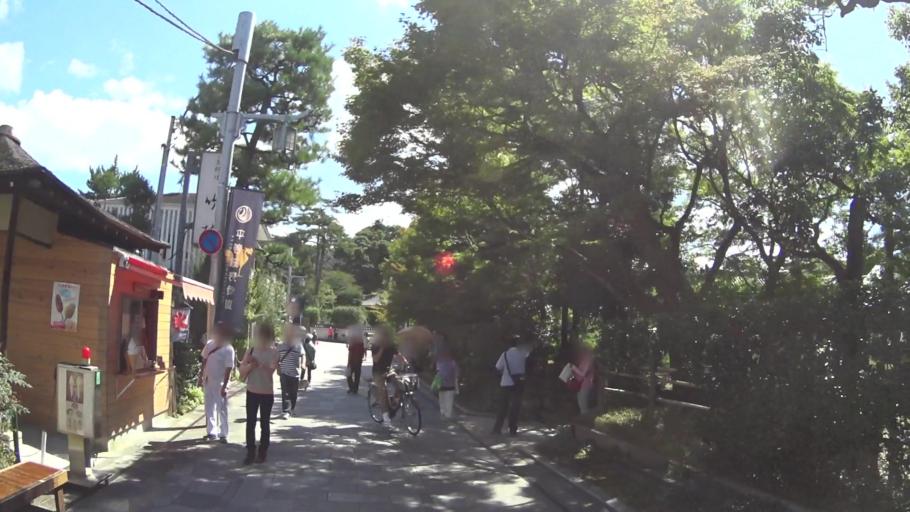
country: JP
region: Kyoto
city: Uji
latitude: 34.8906
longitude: 135.8069
